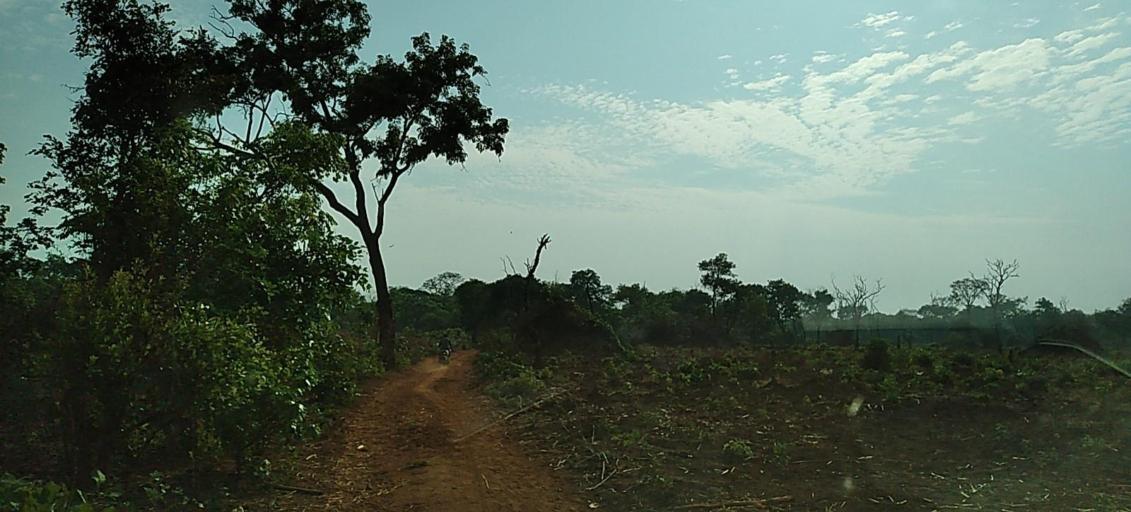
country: ZM
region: Copperbelt
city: Kalulushi
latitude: -12.9641
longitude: 27.7042
